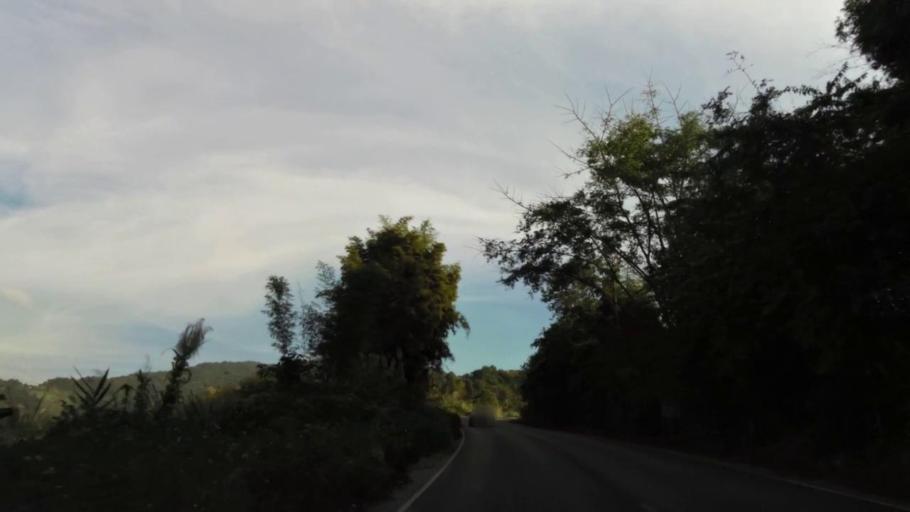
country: TH
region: Chiang Rai
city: Khun Tan
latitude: 19.8650
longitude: 100.4221
